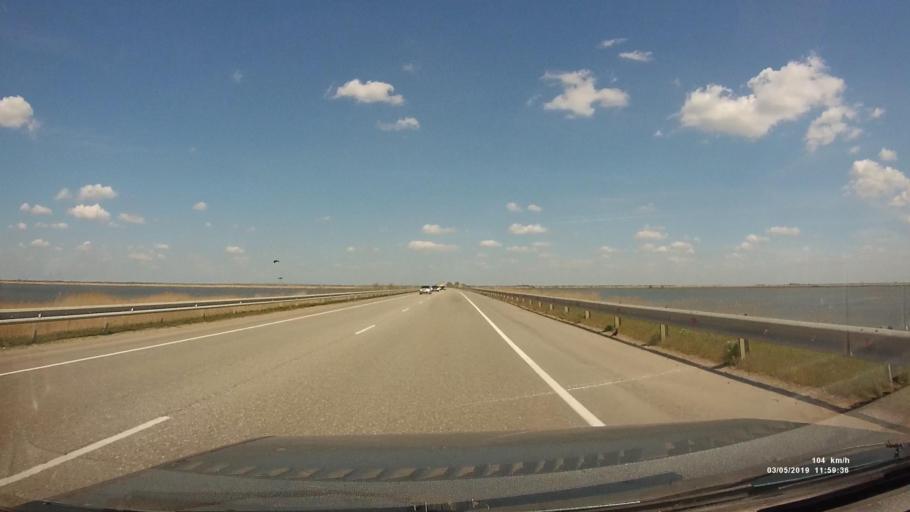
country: RU
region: Rostov
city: Bagayevskaya
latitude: 47.2370
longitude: 40.3318
